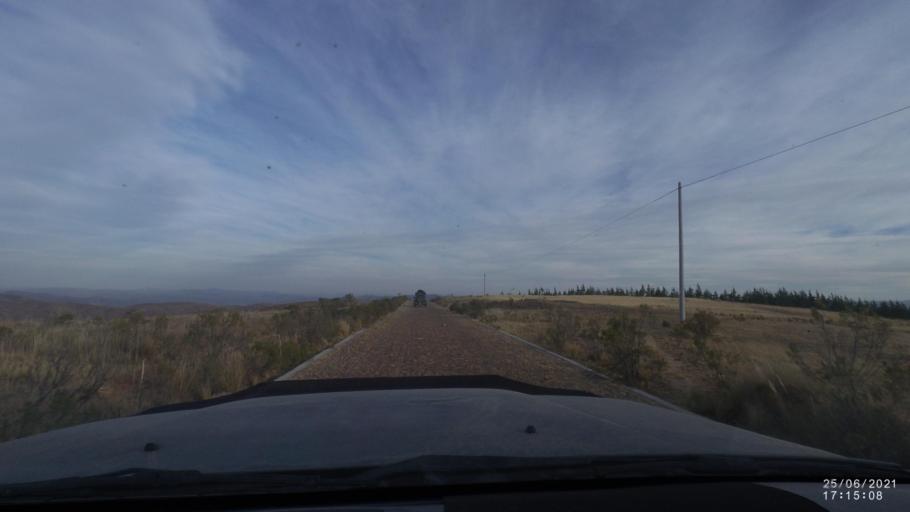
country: BO
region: Cochabamba
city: Arani
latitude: -17.8718
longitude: -65.6987
